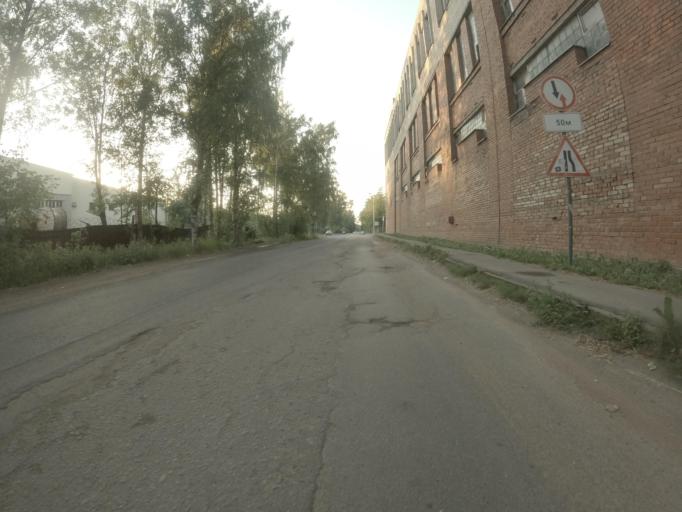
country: RU
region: St.-Petersburg
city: Krasnogvargeisky
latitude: 59.9475
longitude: 30.4415
